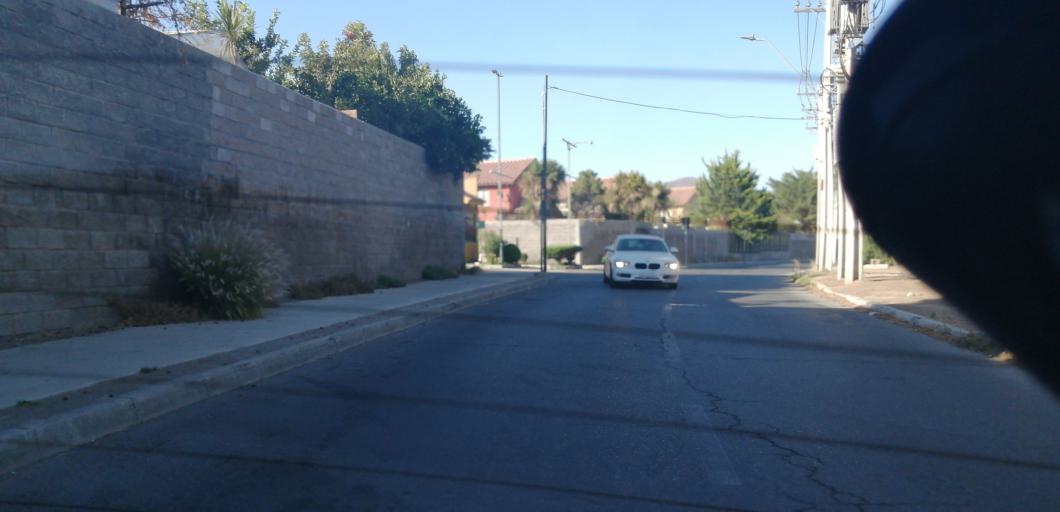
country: CL
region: Santiago Metropolitan
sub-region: Provincia de Santiago
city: Lo Prado
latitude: -33.4550
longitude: -70.8545
